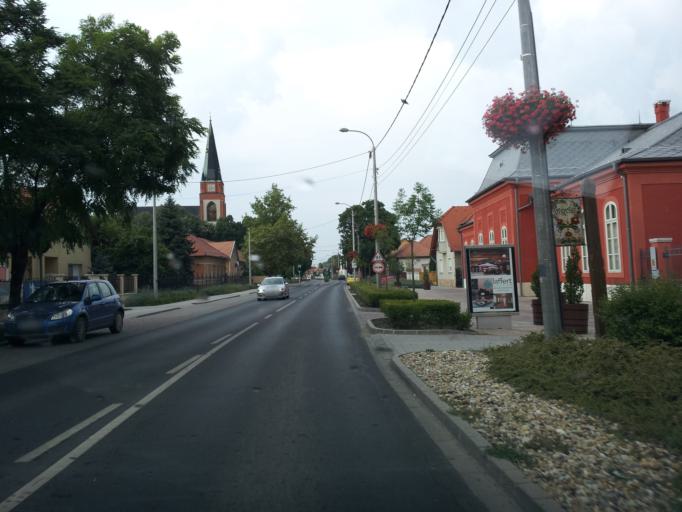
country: HU
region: Pest
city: Dunaharaszti
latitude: 47.3519
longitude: 19.0818
